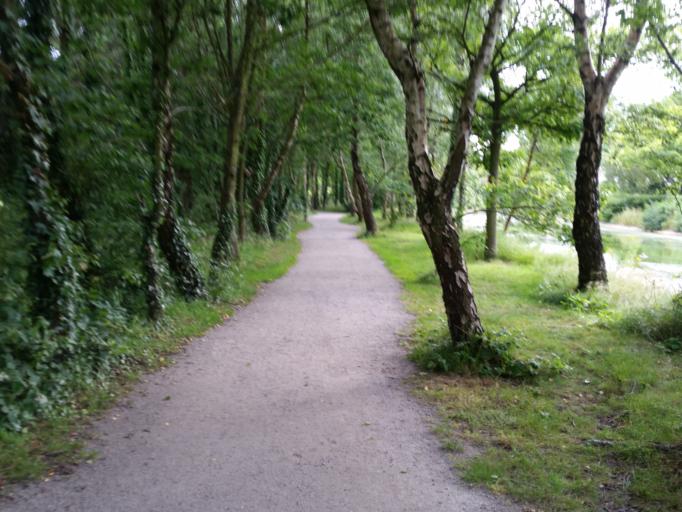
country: GB
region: Northern Ireland
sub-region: Castlereagh District
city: Castlereagh
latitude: 54.6076
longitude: -5.8900
